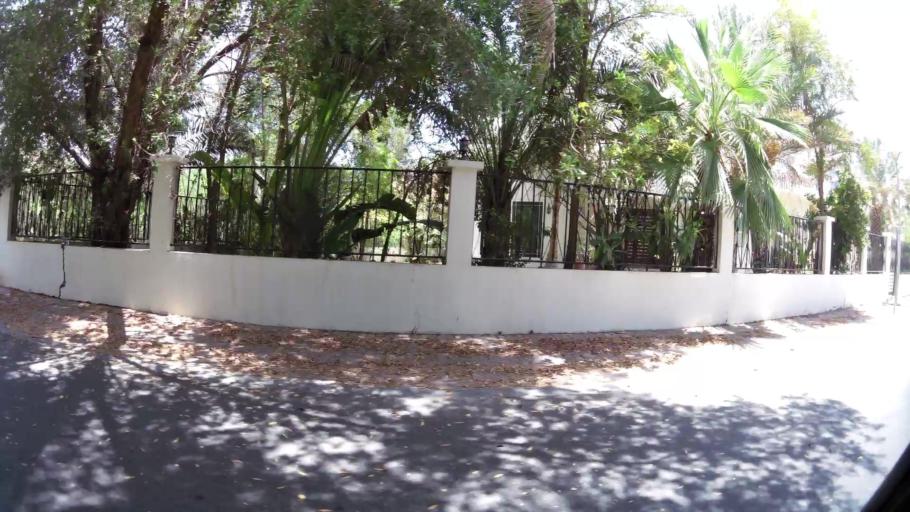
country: OM
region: Muhafazat Masqat
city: Bawshar
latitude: 23.5988
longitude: 58.4595
